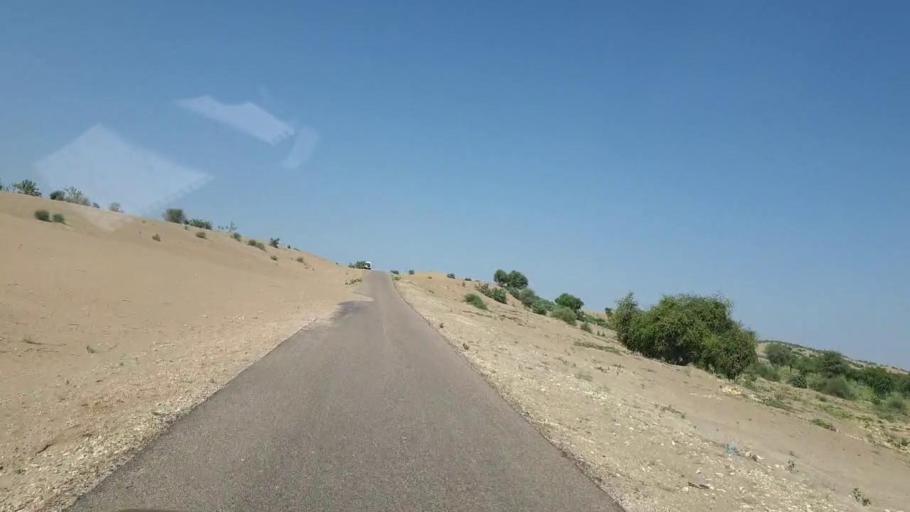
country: PK
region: Sindh
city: Chor
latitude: 25.6133
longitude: 70.3173
